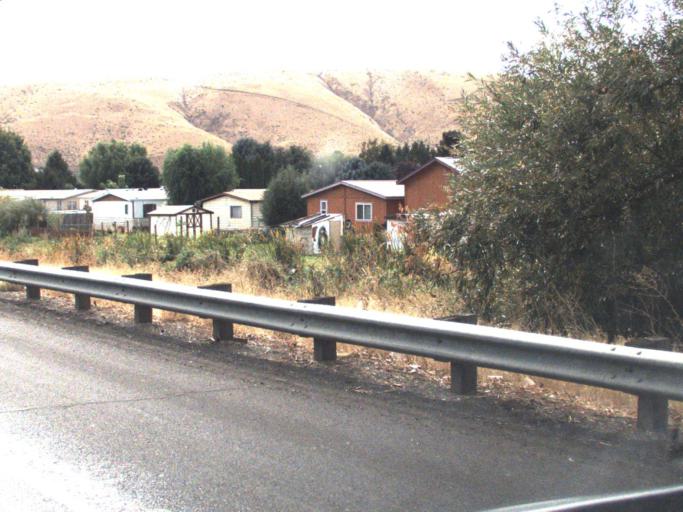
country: US
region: Washington
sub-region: Yakima County
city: Union Gap
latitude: 46.5479
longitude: -120.4707
